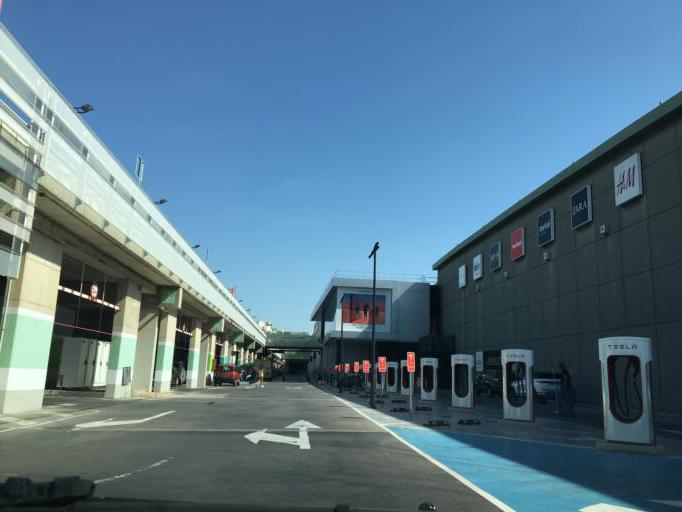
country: ES
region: Murcia
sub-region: Murcia
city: Murcia
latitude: 38.0379
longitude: -1.1494
